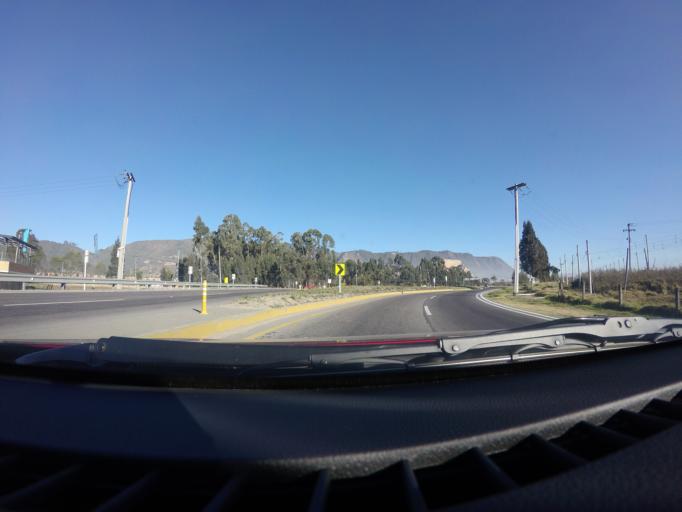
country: CO
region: Cundinamarca
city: Cajica
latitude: 4.9391
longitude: -74.0167
